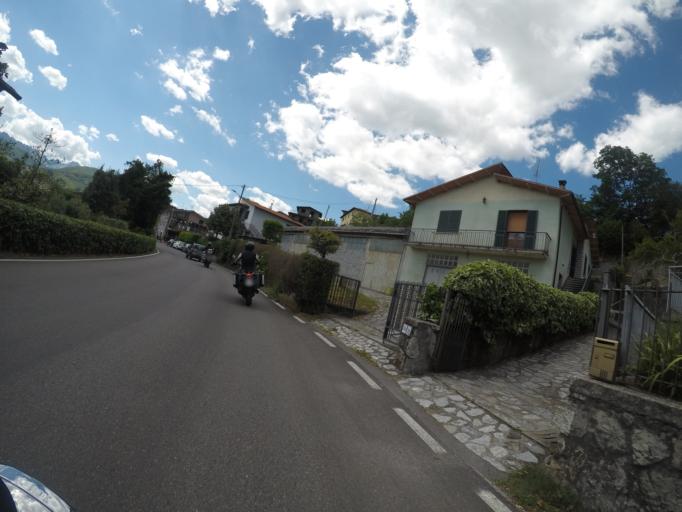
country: IT
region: Tuscany
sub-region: Provincia di Lucca
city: Villa Collemandina
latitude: 44.1487
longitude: 10.3695
